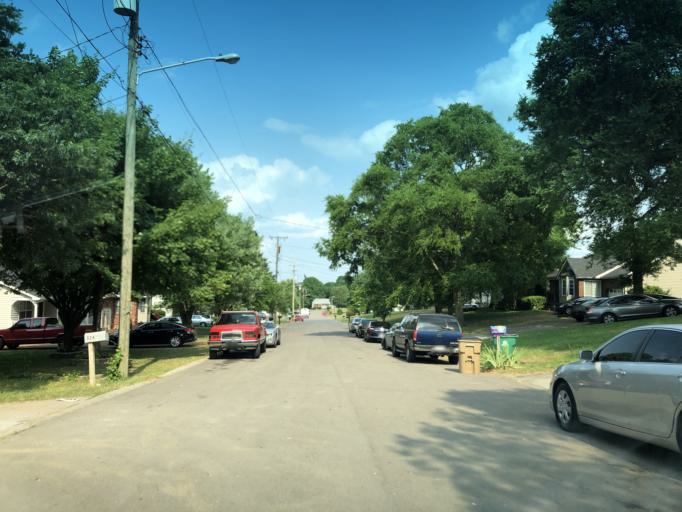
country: US
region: Tennessee
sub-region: Davidson County
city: Goodlettsville
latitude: 36.2744
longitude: -86.7179
